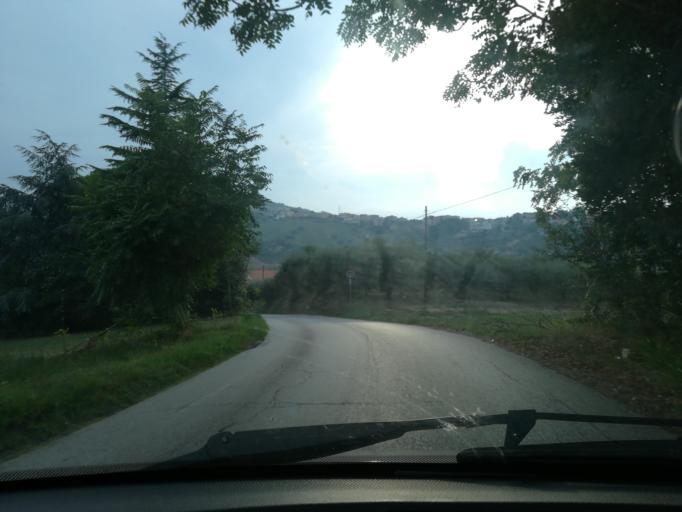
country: IT
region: The Marches
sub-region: Provincia di Macerata
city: Macerata
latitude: 43.3080
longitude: 13.4744
